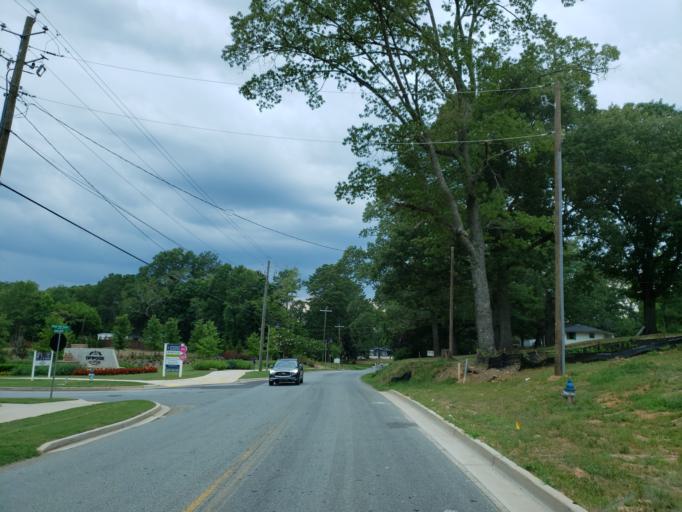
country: US
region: Georgia
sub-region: Cherokee County
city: Woodstock
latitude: 34.1133
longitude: -84.5279
